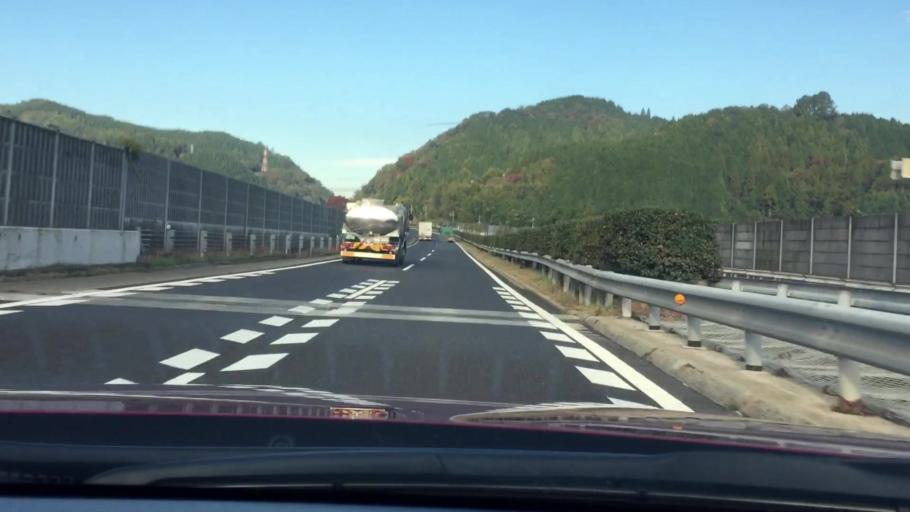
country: JP
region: Hyogo
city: Yamazakicho-nakabirose
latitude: 34.9774
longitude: 134.6345
